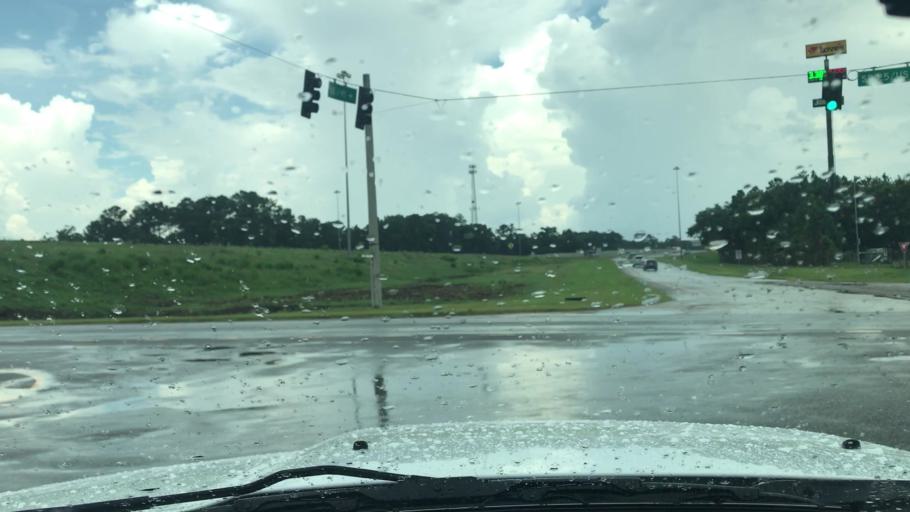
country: US
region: Georgia
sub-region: Glynn County
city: Brunswick
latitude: 31.1372
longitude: -81.5739
